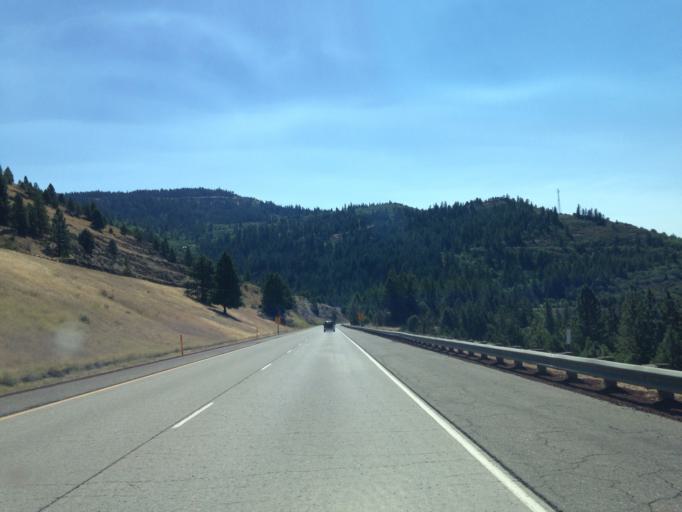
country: US
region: Oregon
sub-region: Jackson County
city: Ashland
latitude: 42.0438
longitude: -122.6035
